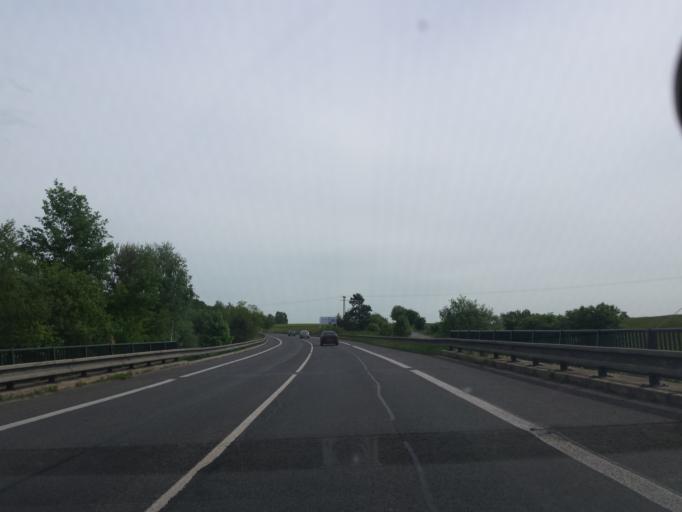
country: CZ
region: Liberecky
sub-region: Okres Ceska Lipa
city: Ceska Lipa
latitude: 50.6512
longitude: 14.5341
